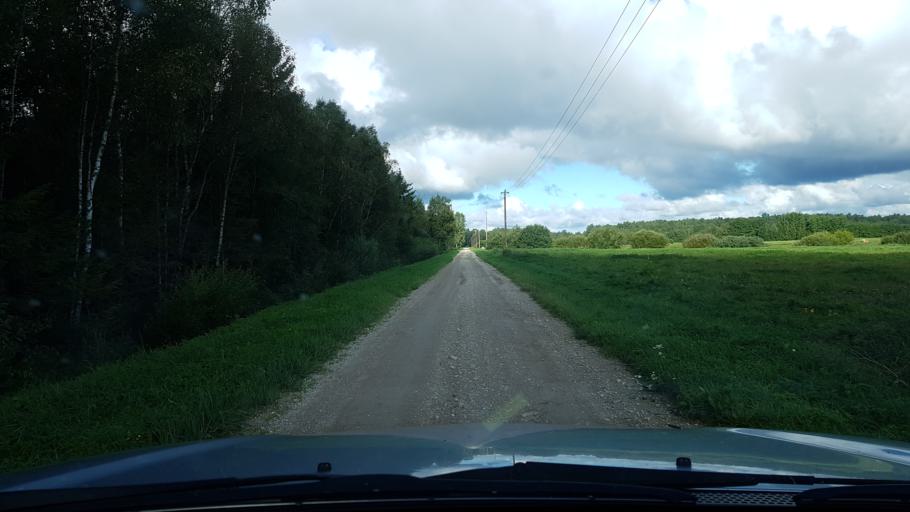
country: EE
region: Harju
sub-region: Rae vald
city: Vaida
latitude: 59.2499
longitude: 25.0699
